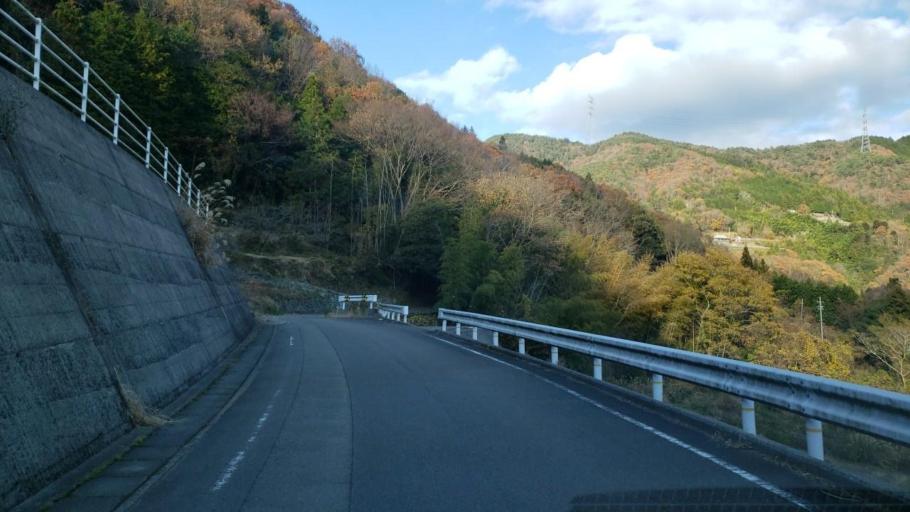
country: JP
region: Tokushima
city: Wakimachi
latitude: 34.1091
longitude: 134.0759
